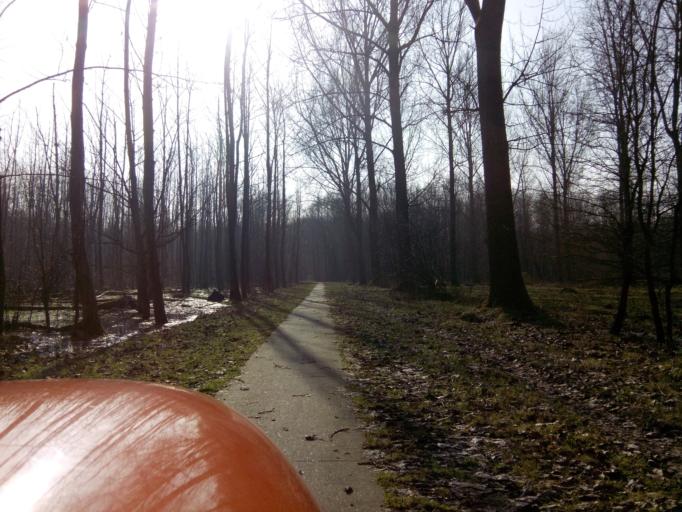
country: NL
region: Utrecht
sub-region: Gemeente Bunschoten
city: Bunschoten
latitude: 52.2615
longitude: 5.4167
